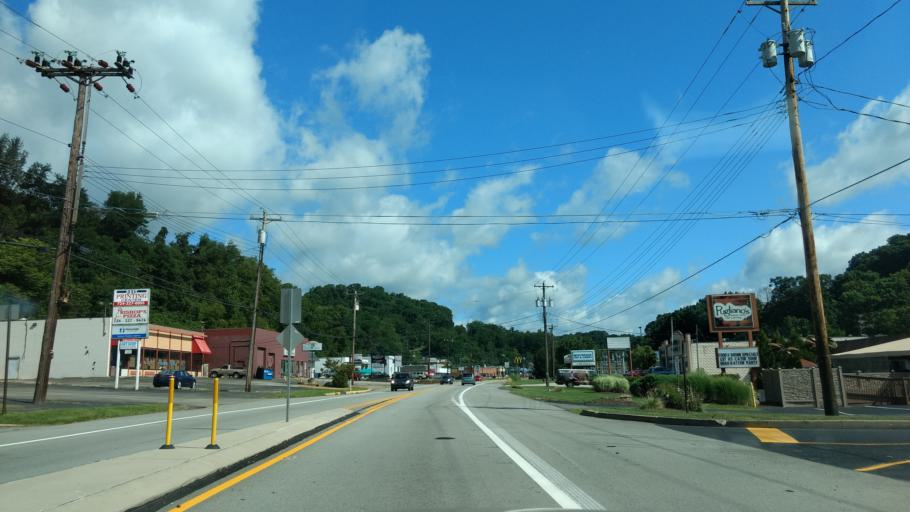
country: US
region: Pennsylvania
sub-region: Westmoreland County
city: Murrysville
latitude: 40.4469
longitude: -79.7139
